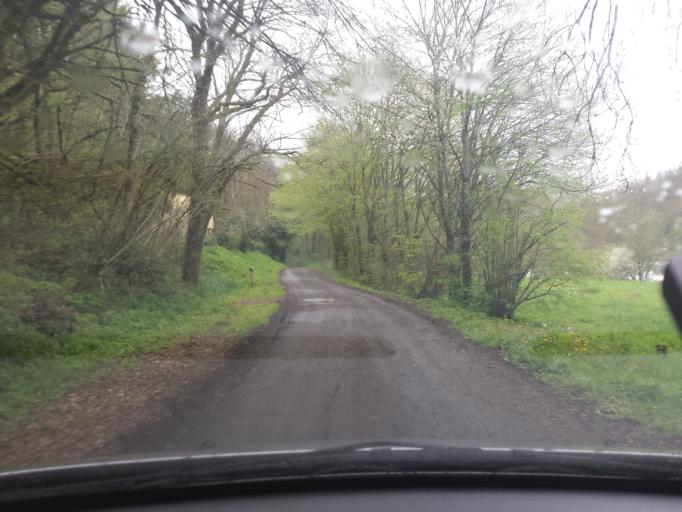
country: FR
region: Pays de la Loire
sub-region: Departement de la Vendee
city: Sainte-Hermine
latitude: 46.5925
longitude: -1.0873
